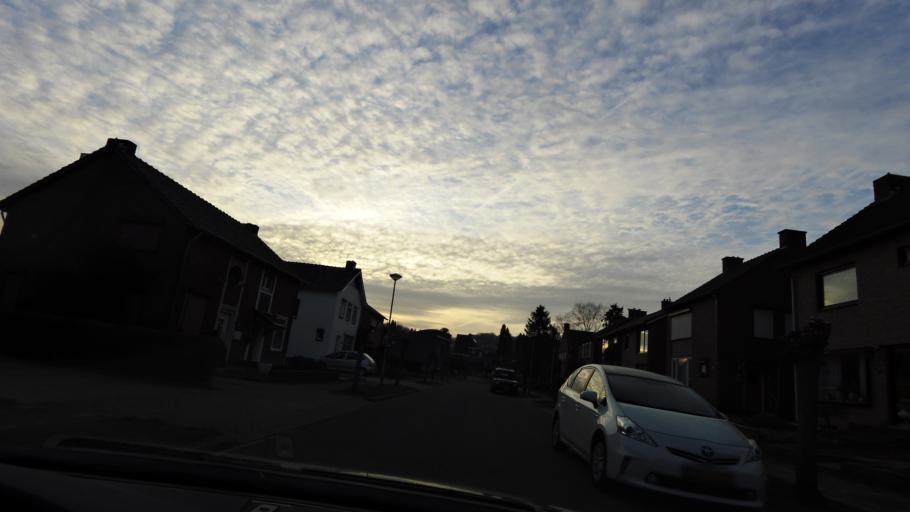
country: NL
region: Limburg
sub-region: Gemeente Schinnen
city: Puth
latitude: 50.9365
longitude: 5.8397
